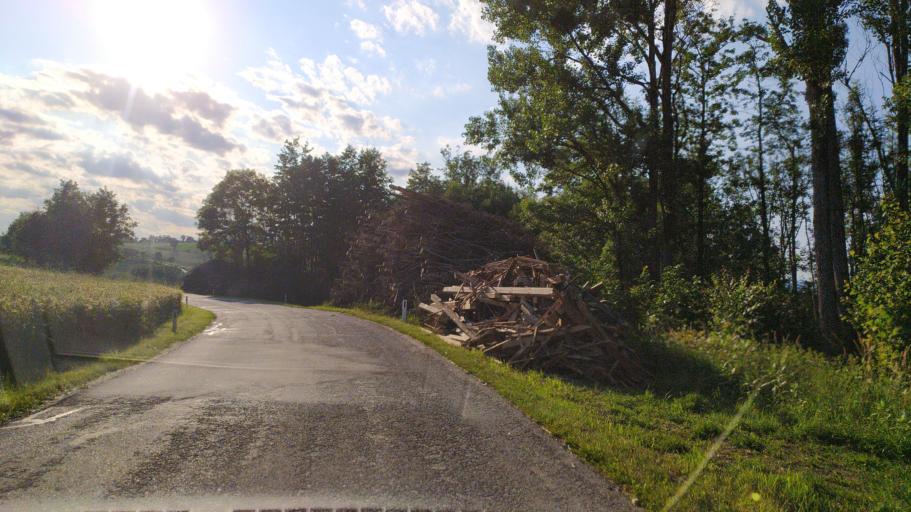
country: AT
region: Lower Austria
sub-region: Politischer Bezirk Amstetten
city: Strengberg
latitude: 48.1487
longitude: 14.6884
